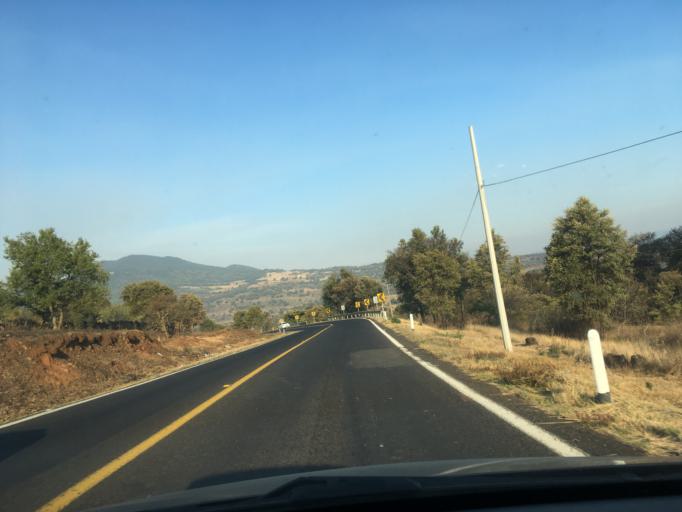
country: MX
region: Michoacan
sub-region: Morelia
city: Iratzio
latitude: 19.6283
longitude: -101.4351
